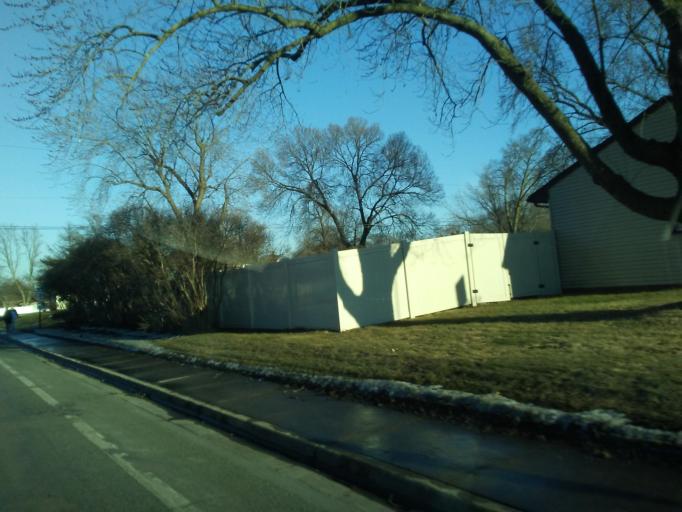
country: US
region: Minnesota
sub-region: Hennepin County
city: Bloomington
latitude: 44.8479
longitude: -93.2757
